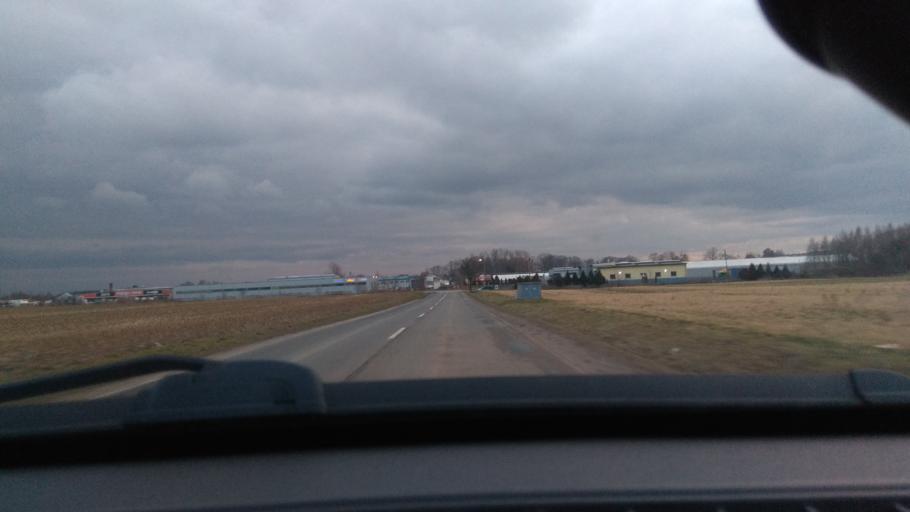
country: PL
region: Greater Poland Voivodeship
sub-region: Powiat kepinski
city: Kepno
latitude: 51.2907
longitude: 18.0061
